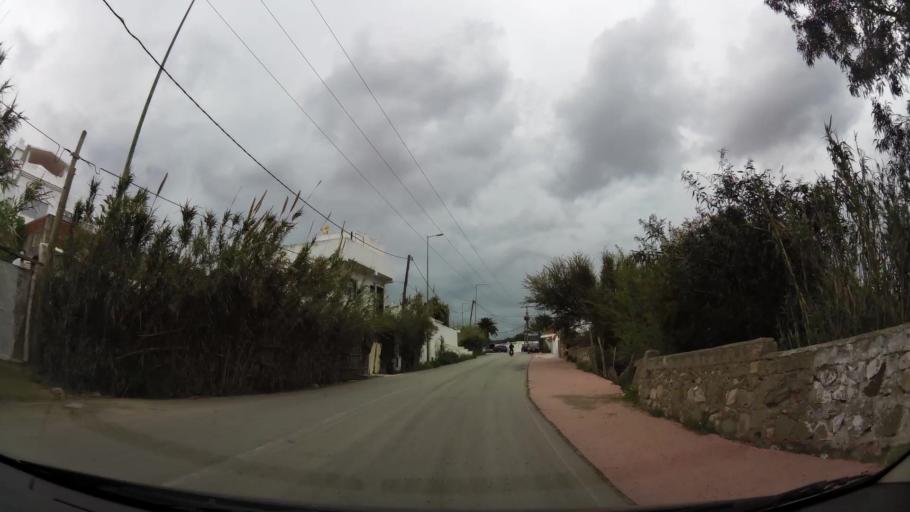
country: MA
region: Tanger-Tetouan
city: Tetouan
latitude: 35.5515
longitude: -5.3643
